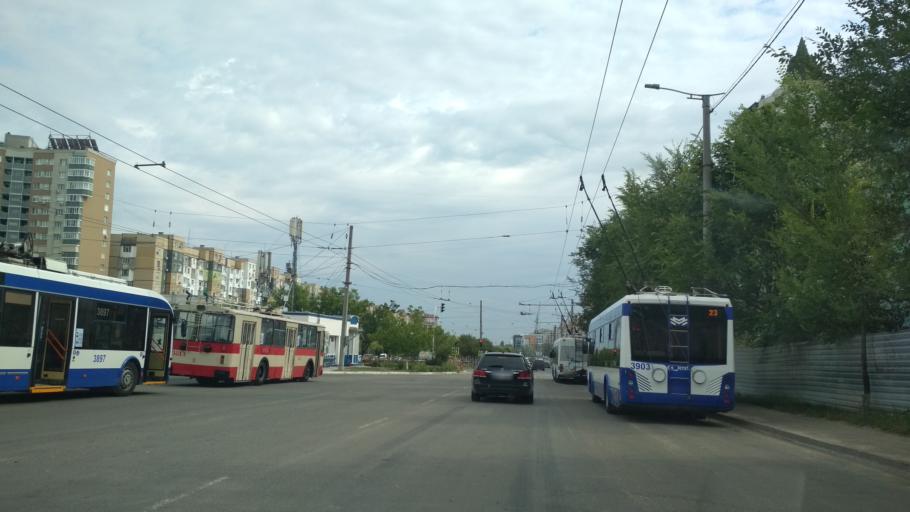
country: MD
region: Chisinau
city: Stauceni
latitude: 47.0574
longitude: 28.8911
